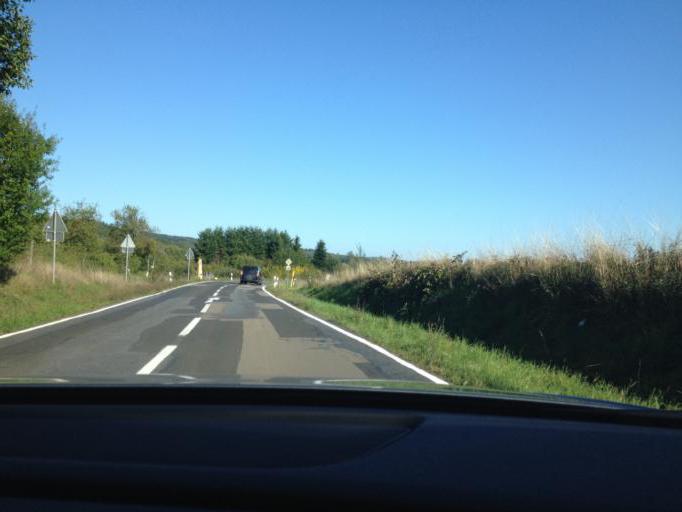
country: DE
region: Saarland
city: Mainzweiler
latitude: 49.4296
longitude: 7.1186
